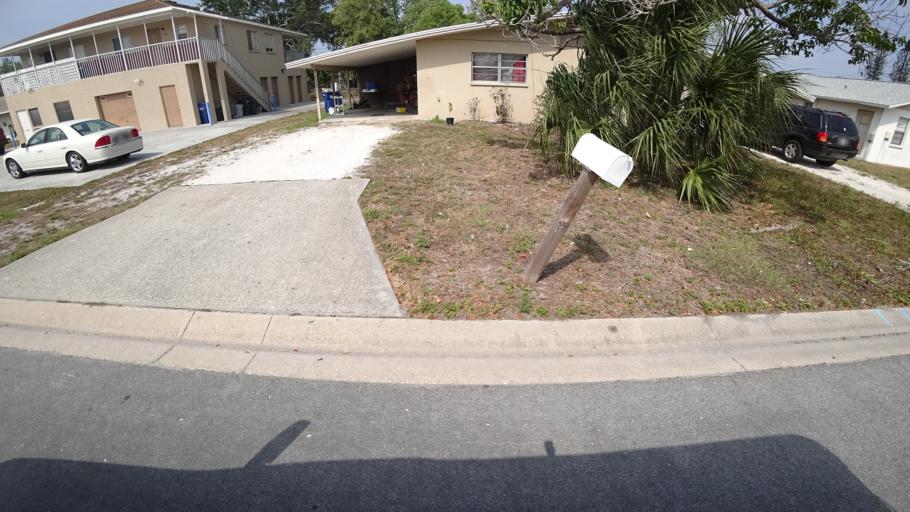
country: US
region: Florida
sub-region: Manatee County
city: West Bradenton
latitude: 27.4641
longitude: -82.6238
